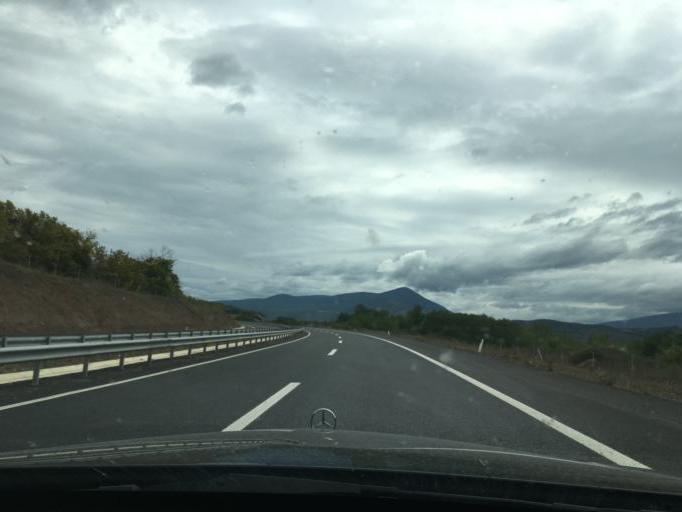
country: RS
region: Central Serbia
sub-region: Pirotski Okrug
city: Bela Palanka
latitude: 43.2509
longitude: 22.2707
